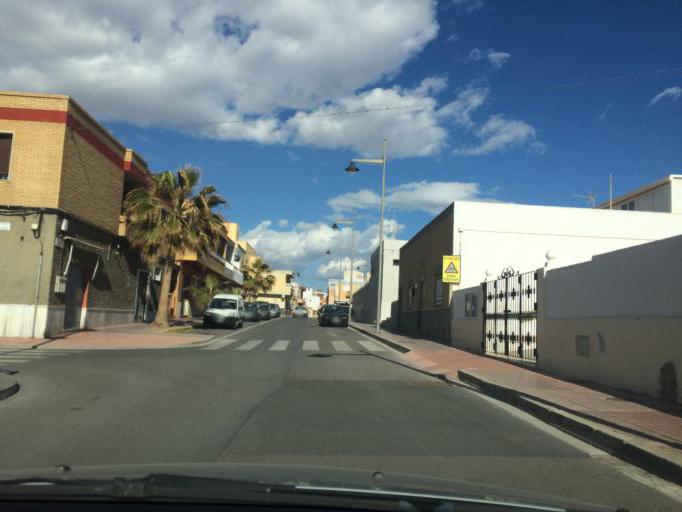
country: ES
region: Andalusia
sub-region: Provincia de Almeria
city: Retamar
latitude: 36.7805
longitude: -2.2431
